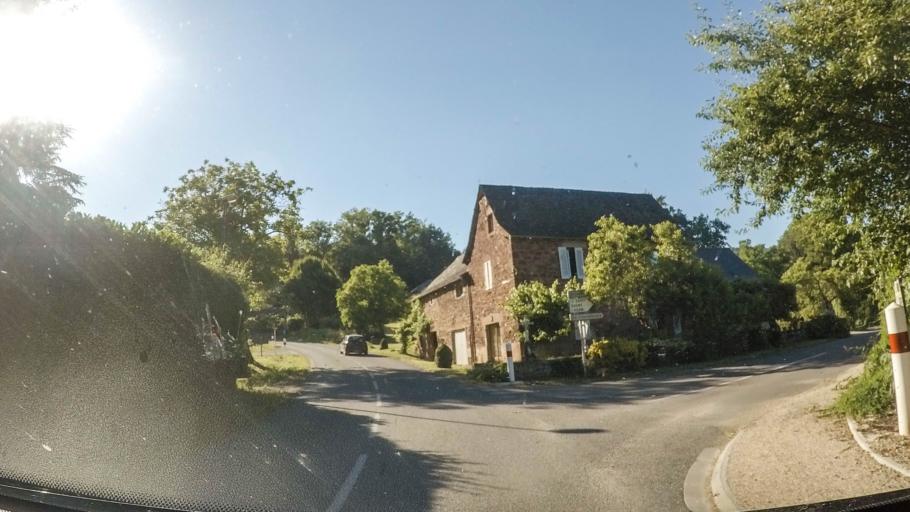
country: FR
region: Midi-Pyrenees
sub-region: Departement de l'Aveyron
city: Saint-Christophe-Vallon
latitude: 44.5501
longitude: 2.4033
